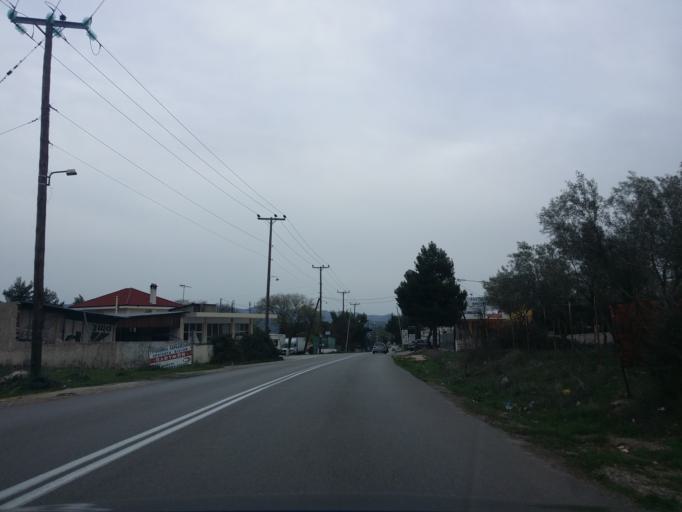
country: GR
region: Attica
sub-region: Nomarchia Dytikis Attikis
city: Vilia
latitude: 38.1662
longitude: 23.4136
